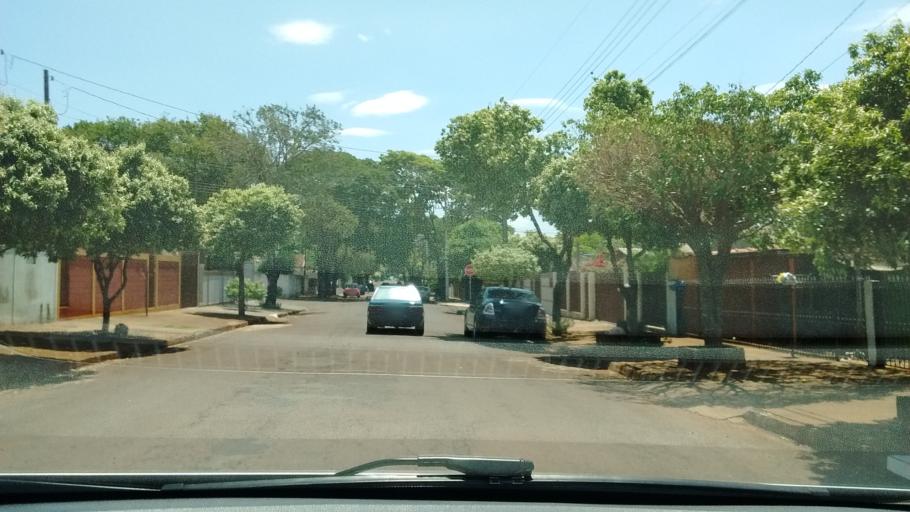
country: BR
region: Parana
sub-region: Corbelia
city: Corbelia
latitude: -24.5373
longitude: -52.9911
